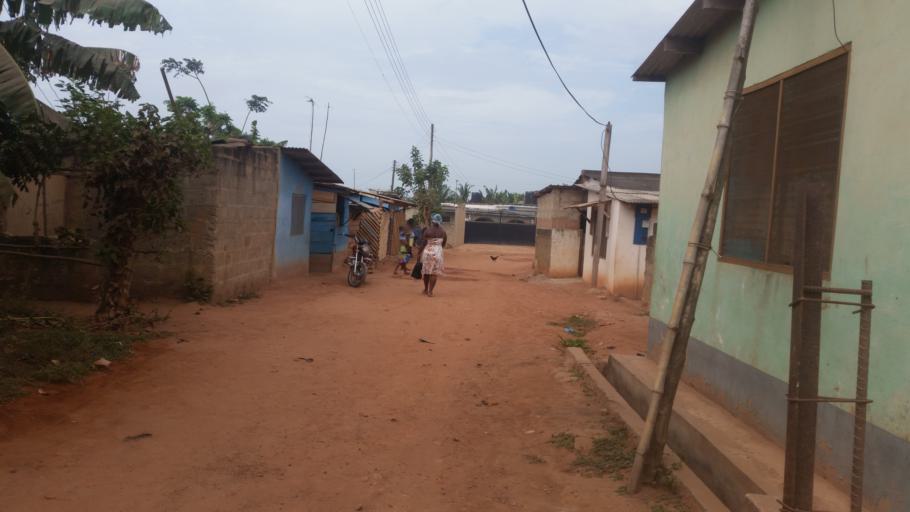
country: GH
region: Central
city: Cape Coast
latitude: 5.1239
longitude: -1.3036
